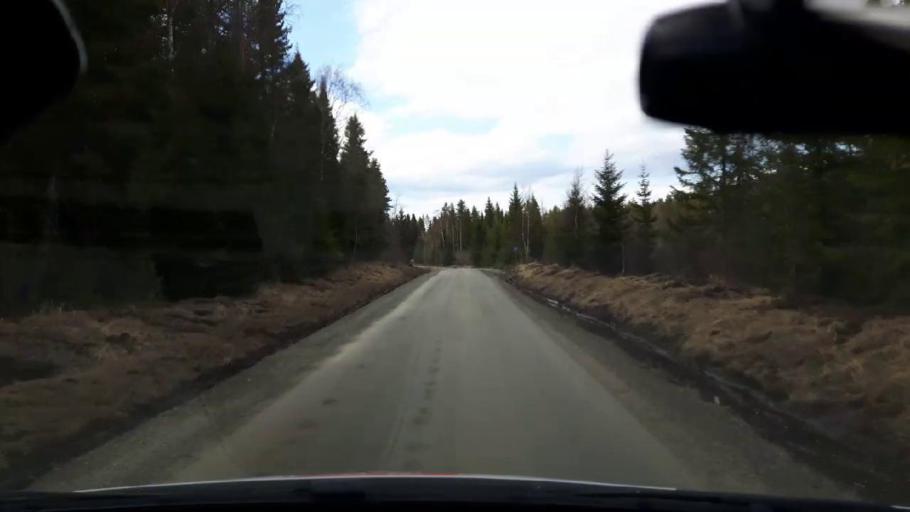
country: SE
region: Jaemtland
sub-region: Bergs Kommun
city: Hoverberg
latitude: 62.9054
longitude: 14.6377
